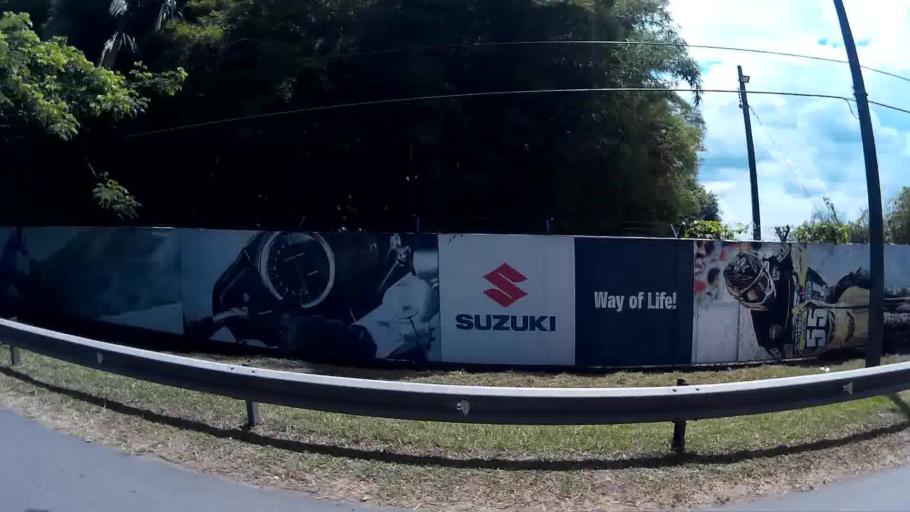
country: CO
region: Valle del Cauca
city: Cartago
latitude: 4.8064
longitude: -75.8212
